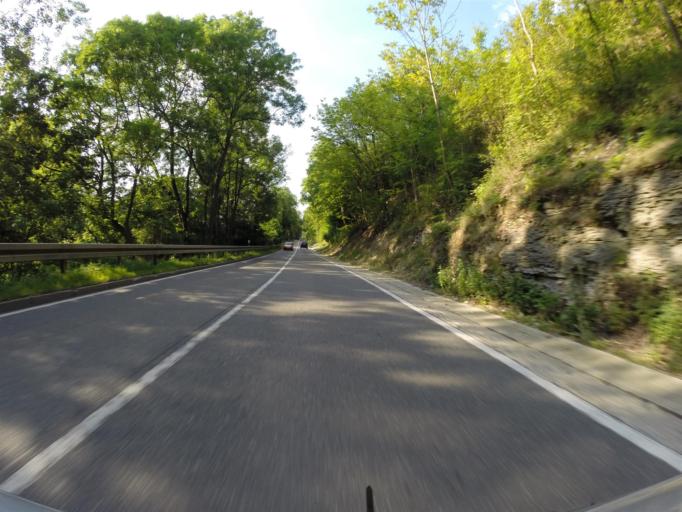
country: DE
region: Thuringia
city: Wichmar
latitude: 51.0190
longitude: 11.6920
